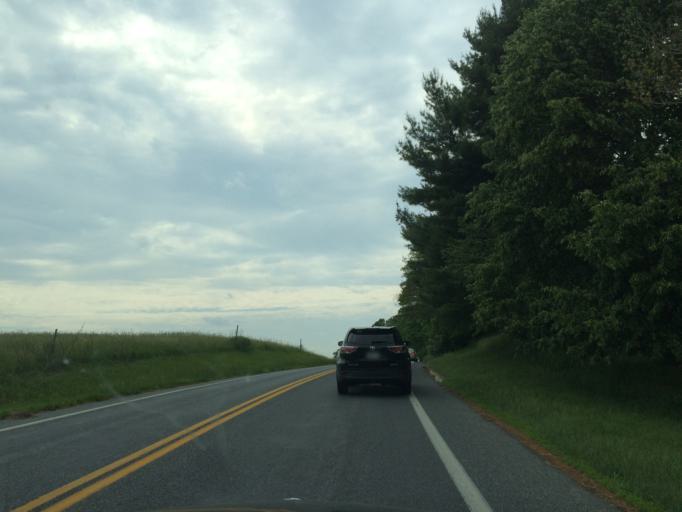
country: US
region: Maryland
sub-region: Howard County
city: Highland
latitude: 39.2466
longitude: -76.9197
